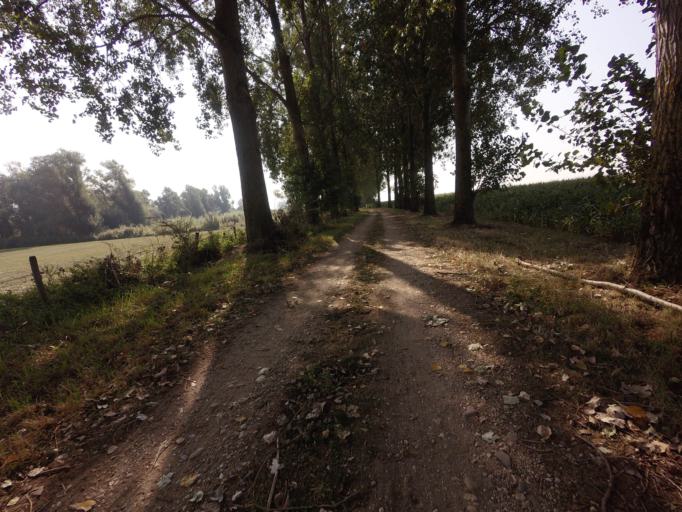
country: NL
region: Limburg
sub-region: Gemeente Roermond
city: Leeuwen
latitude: 51.2401
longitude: 5.9989
